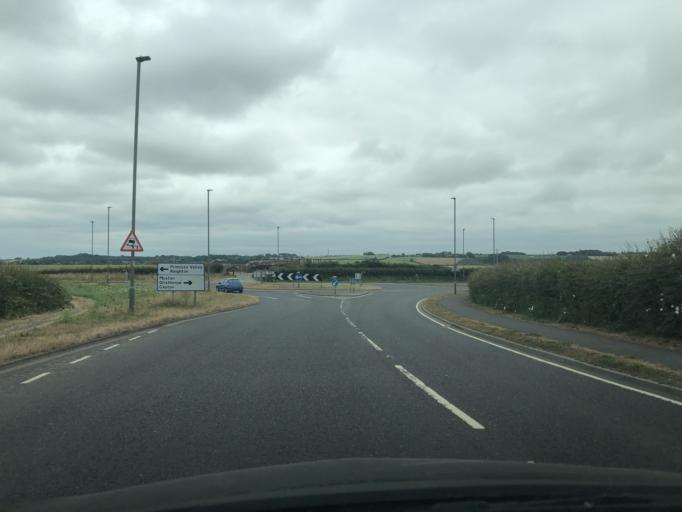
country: GB
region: England
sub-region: North Yorkshire
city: Filey
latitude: 54.2001
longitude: -0.3057
